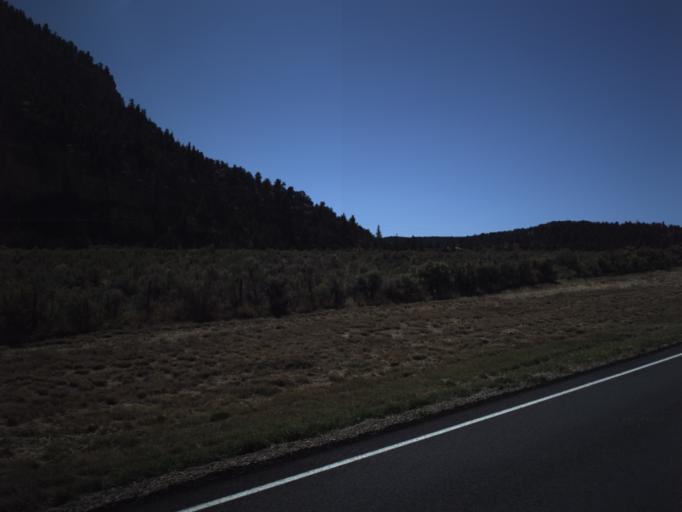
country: US
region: Utah
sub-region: Garfield County
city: Panguitch
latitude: 37.7270
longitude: -111.7720
